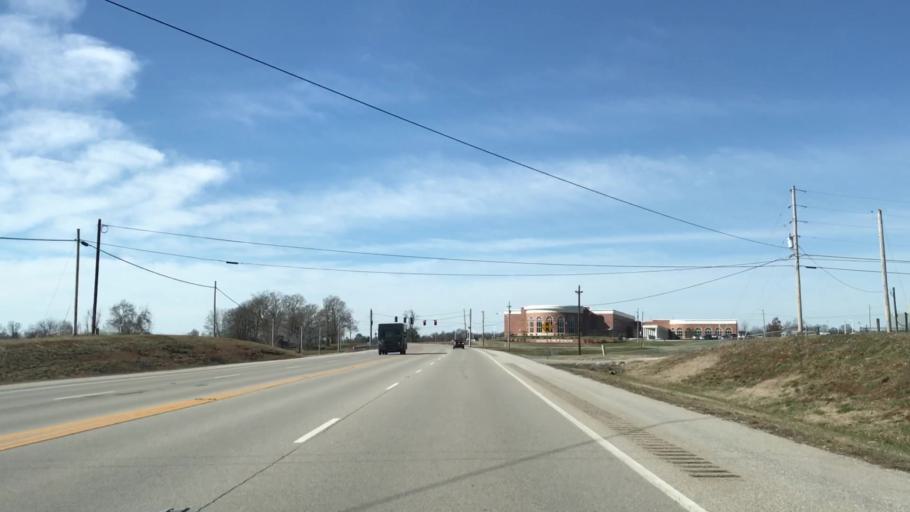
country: US
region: Kentucky
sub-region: Barren County
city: Glasgow
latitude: 37.0093
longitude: -85.8838
